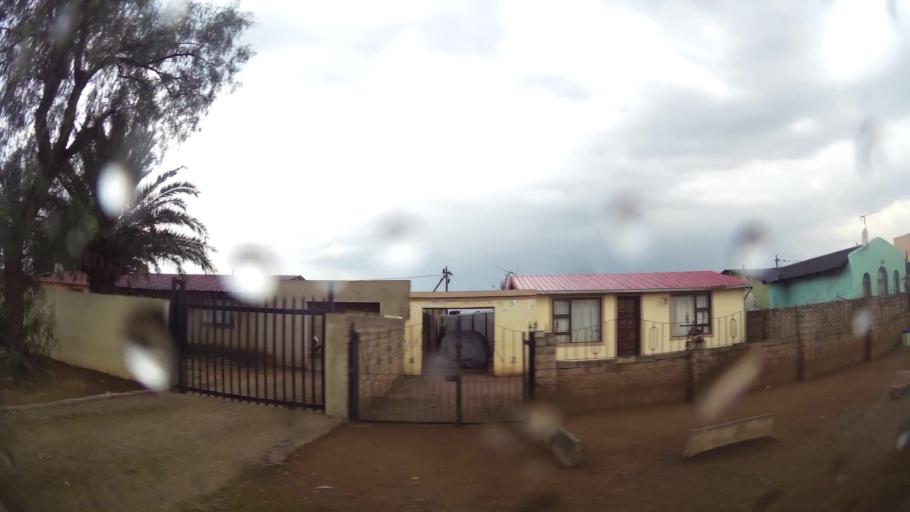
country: ZA
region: Gauteng
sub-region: Ekurhuleni Metropolitan Municipality
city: Germiston
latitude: -26.3772
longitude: 28.1322
